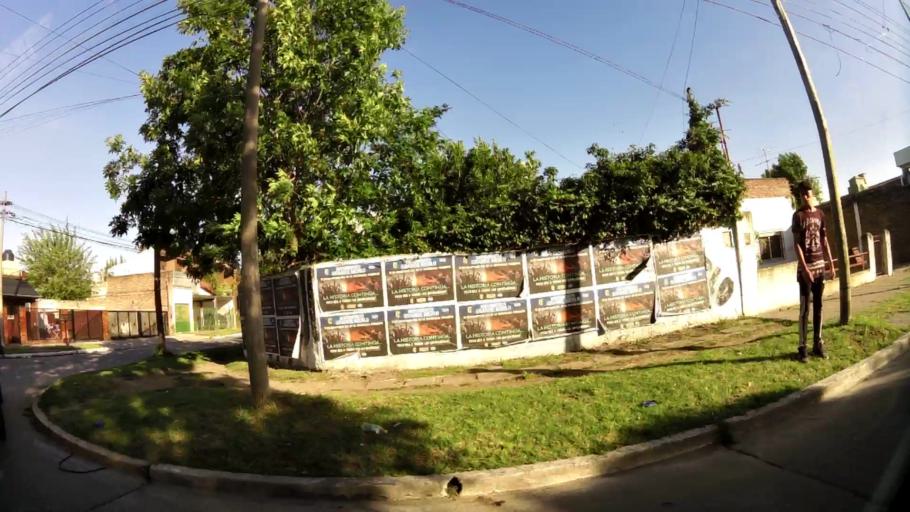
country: AR
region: Buenos Aires
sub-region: Partido de Merlo
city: Merlo
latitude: -34.6842
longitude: -58.7320
